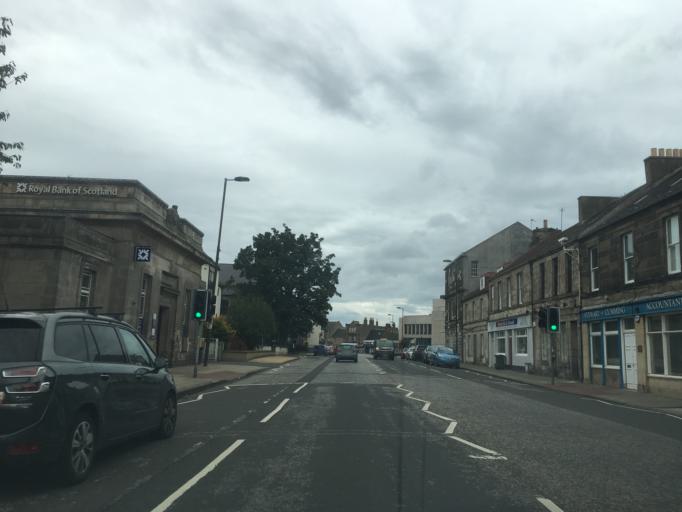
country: GB
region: Scotland
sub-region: East Lothian
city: Musselburgh
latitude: 55.9429
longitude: -3.0559
